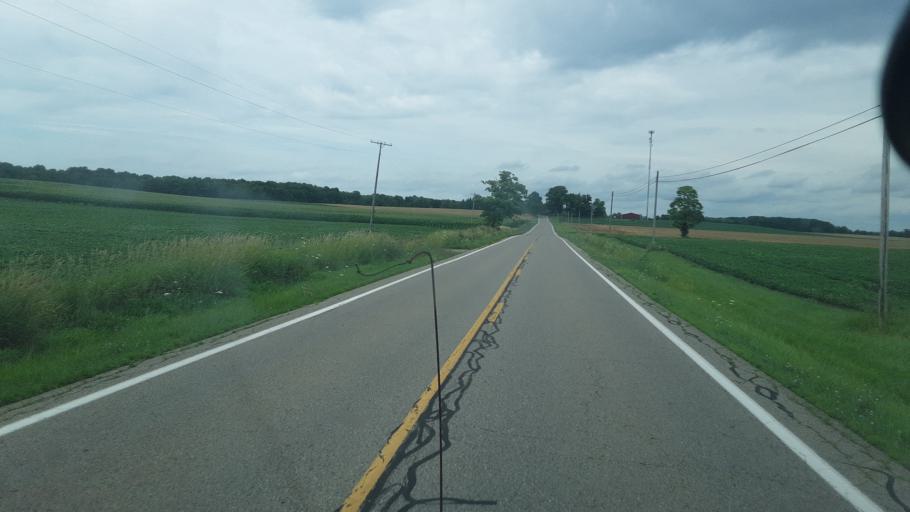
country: US
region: Ohio
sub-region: Trumbull County
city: Cortland
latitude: 41.4351
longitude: -80.6654
